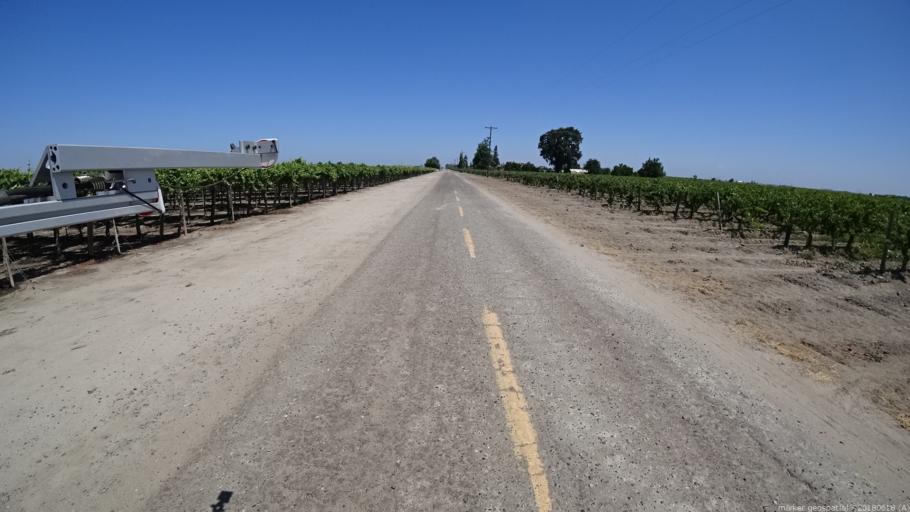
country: US
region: California
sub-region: Madera County
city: Parkwood
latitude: 36.8592
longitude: -120.1194
